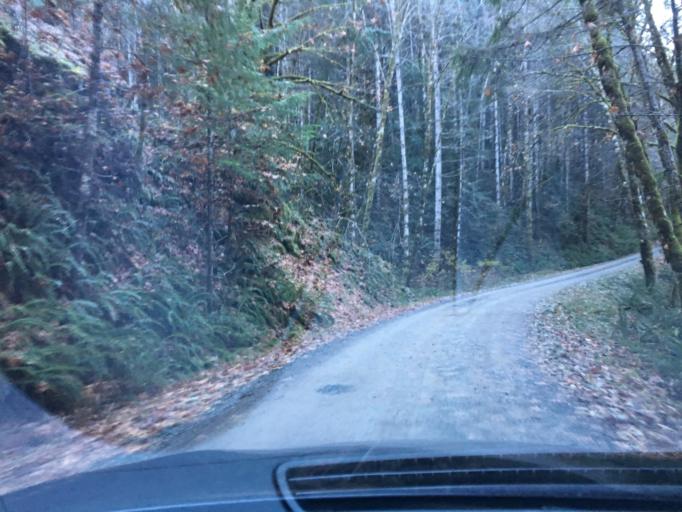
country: US
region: Oregon
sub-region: Douglas County
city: Winston
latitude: 43.3211
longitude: -123.5789
